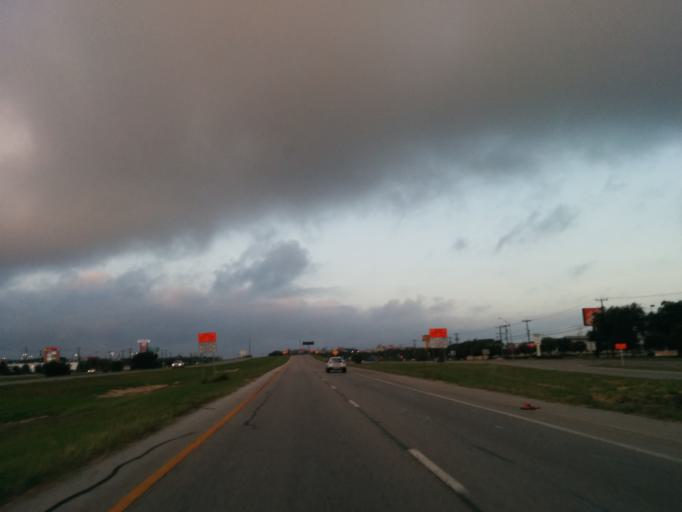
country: US
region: Texas
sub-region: Bexar County
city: Helotes
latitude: 29.5578
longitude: -98.6627
